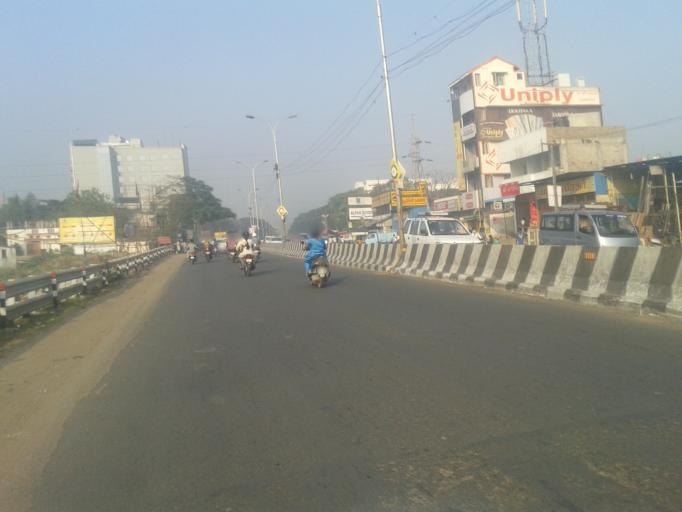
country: IN
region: Tamil Nadu
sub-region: Thiruvallur
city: Porur
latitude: 13.0361
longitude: 80.1475
